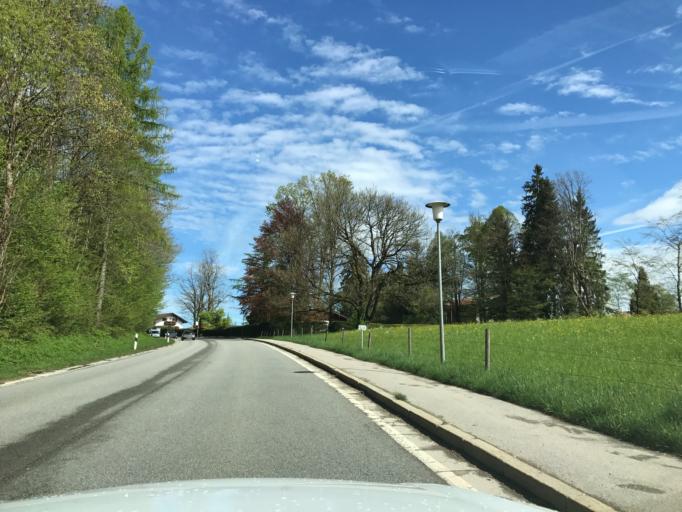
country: DE
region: Bavaria
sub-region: Upper Bavaria
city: Bad Wiessee
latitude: 47.6972
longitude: 11.7318
